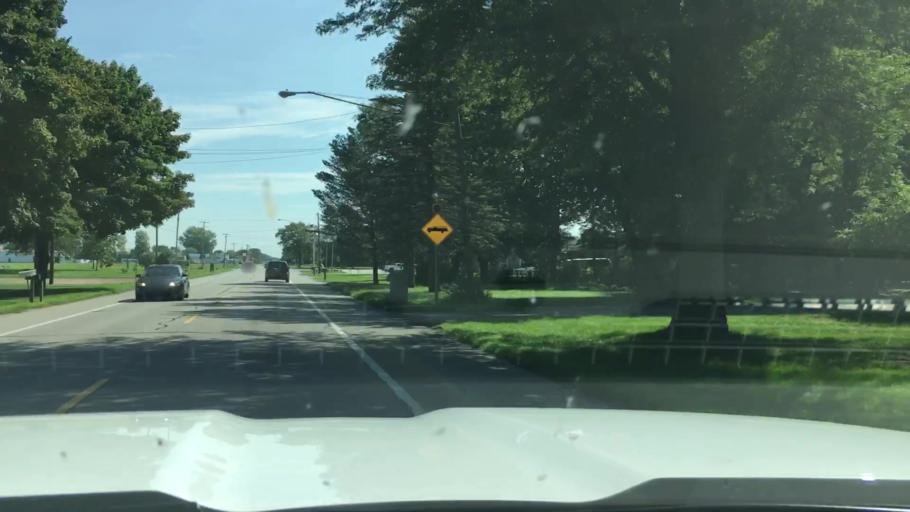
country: US
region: Michigan
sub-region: Bay County
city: Essexville
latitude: 43.5941
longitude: -83.8122
